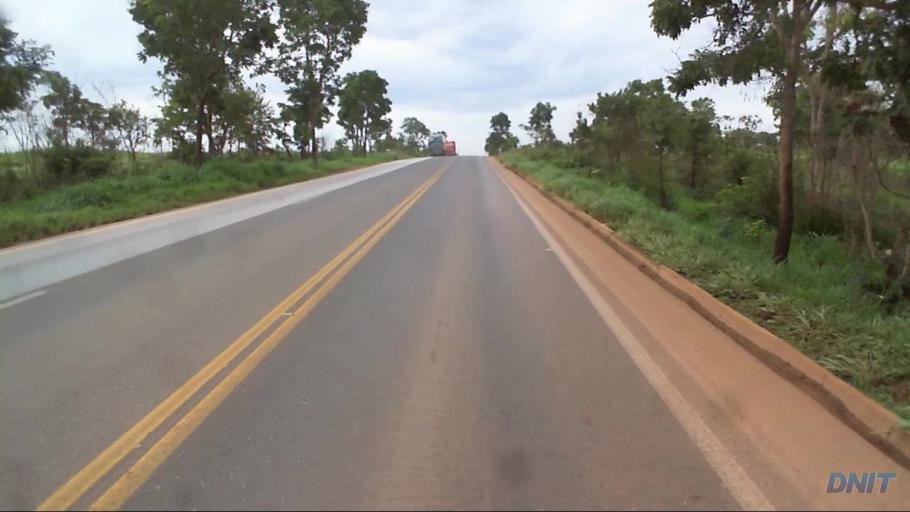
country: BR
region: Goias
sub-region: Uruacu
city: Uruacu
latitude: -14.5823
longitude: -49.1600
